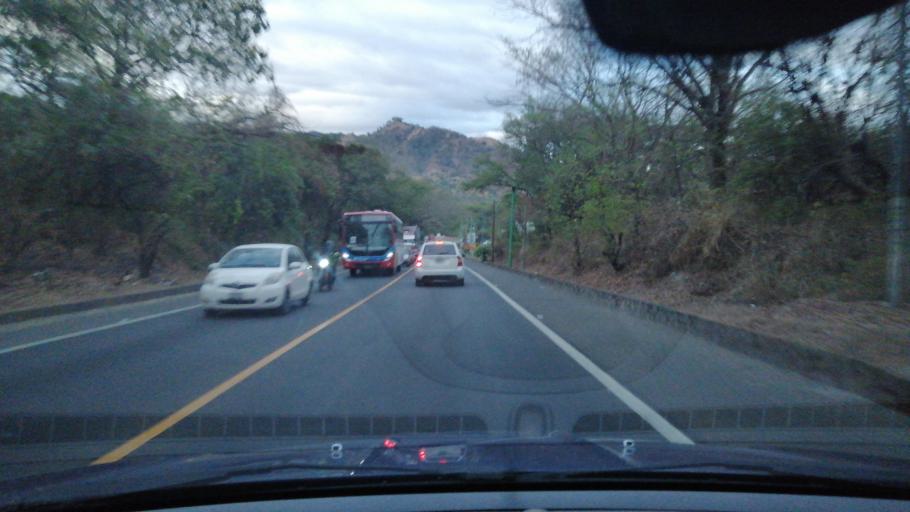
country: SV
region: Santa Ana
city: Santa Ana
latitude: 14.0078
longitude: -89.5423
